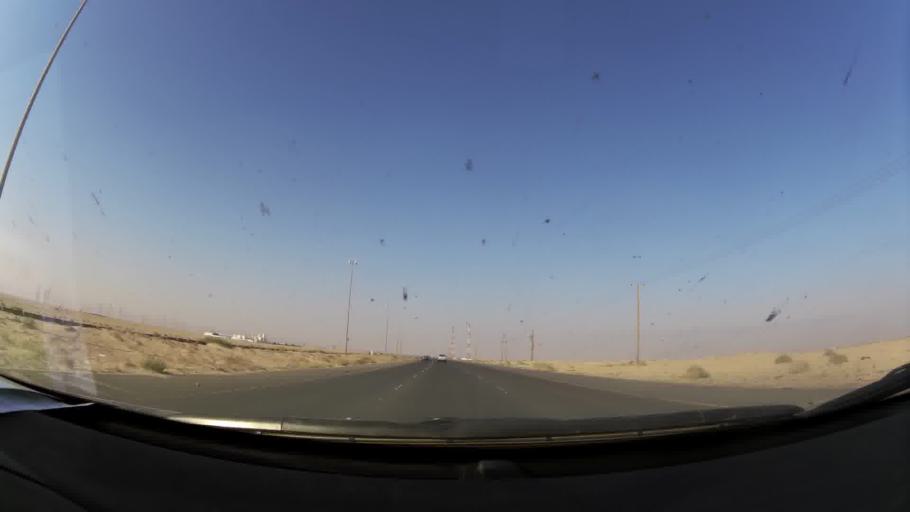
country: IQ
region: Basra Governorate
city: Umm Qasr
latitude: 29.7770
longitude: 47.6724
